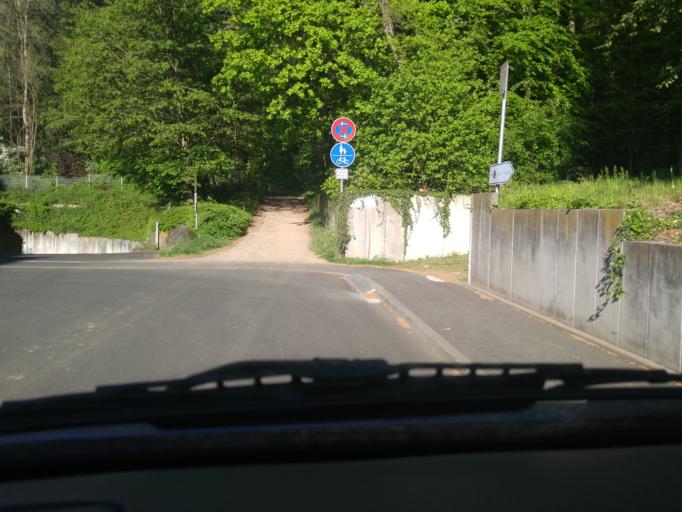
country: DE
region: Hesse
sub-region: Regierungsbezirk Darmstadt
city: Bad Nauheim
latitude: 50.3551
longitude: 8.7278
